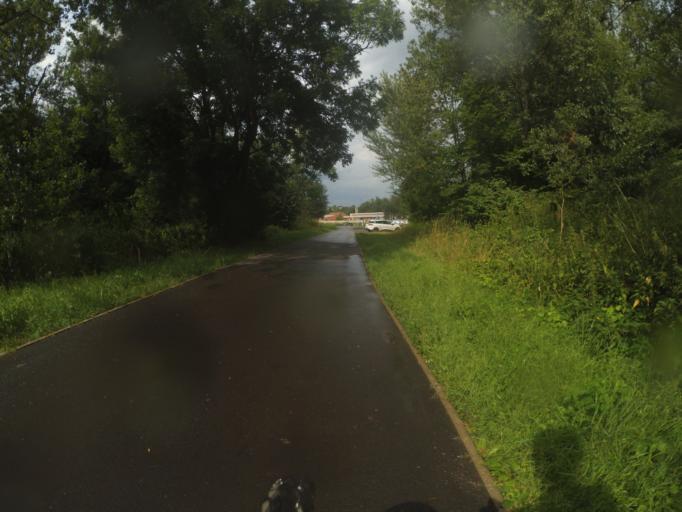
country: CZ
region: Central Bohemia
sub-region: Okres Melnik
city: Melnik
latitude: 50.3512
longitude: 14.4665
